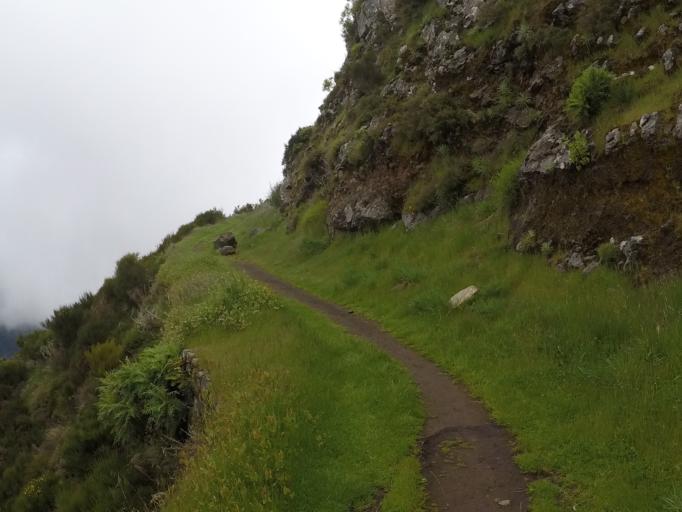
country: PT
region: Madeira
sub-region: Camara de Lobos
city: Curral das Freiras
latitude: 32.7141
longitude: -16.9889
